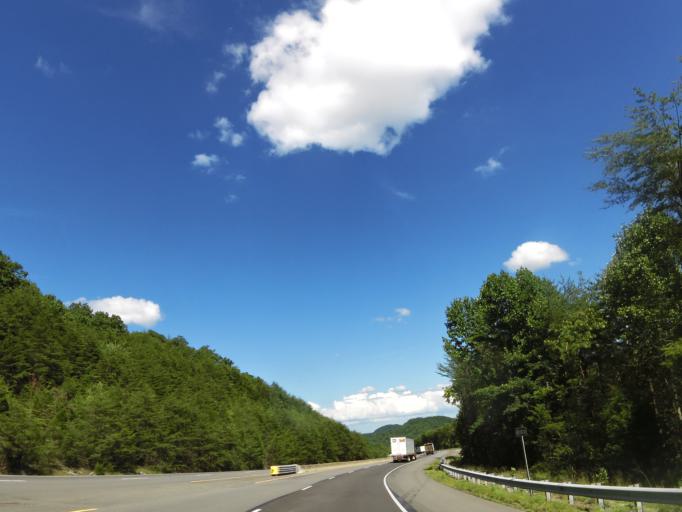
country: US
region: Tennessee
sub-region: Grainger County
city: Bean Station
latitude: 36.3546
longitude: -83.3739
